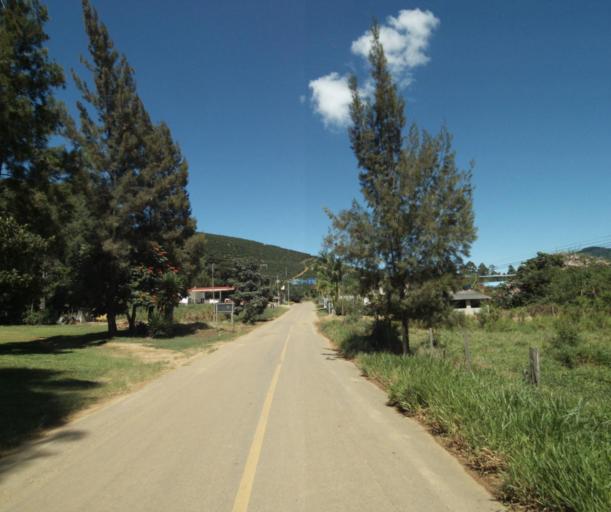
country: BR
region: Minas Gerais
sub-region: Espera Feliz
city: Espera Feliz
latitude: -20.5618
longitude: -41.8238
